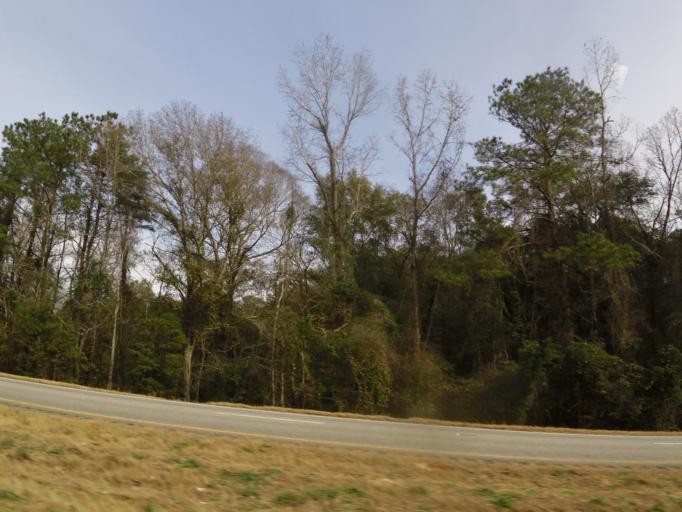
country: US
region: Alabama
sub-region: Dale County
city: Newton
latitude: 31.3560
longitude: -85.5581
